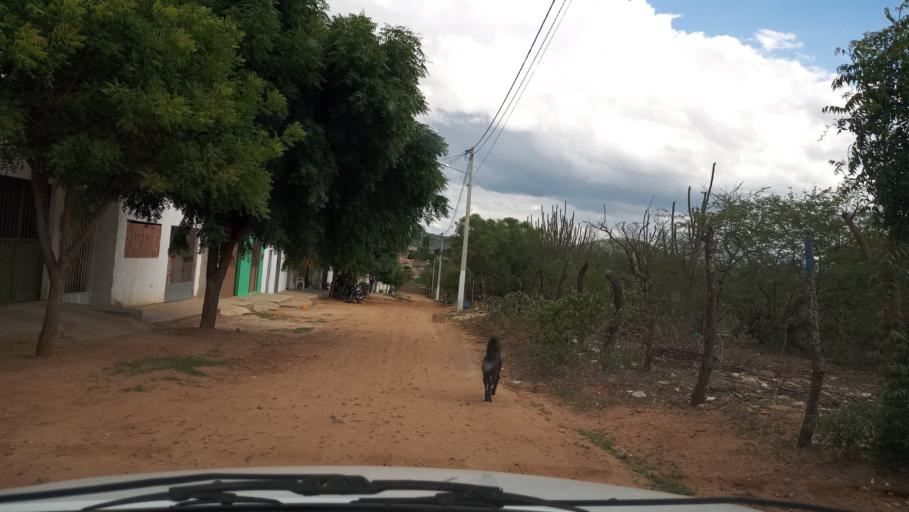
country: BR
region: Rio Grande do Norte
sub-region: Sao Tome
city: Sao Tome
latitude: -5.9423
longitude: -35.9273
